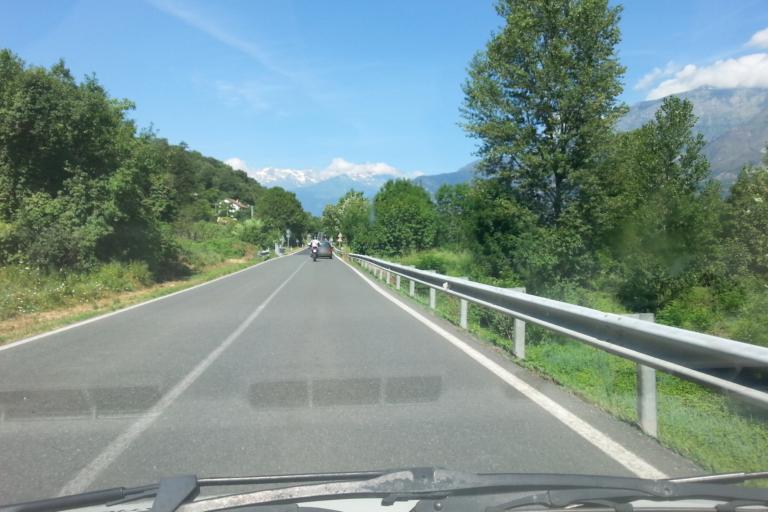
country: IT
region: Piedmont
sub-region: Provincia di Torino
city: San Didero
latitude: 45.1203
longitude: 7.2074
